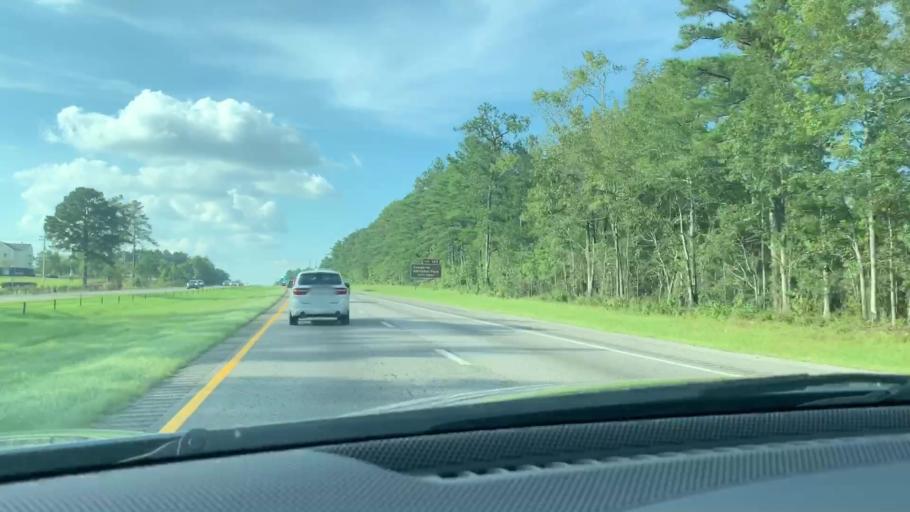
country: US
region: South Carolina
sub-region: Orangeburg County
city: Brookdale
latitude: 33.5532
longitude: -80.8190
